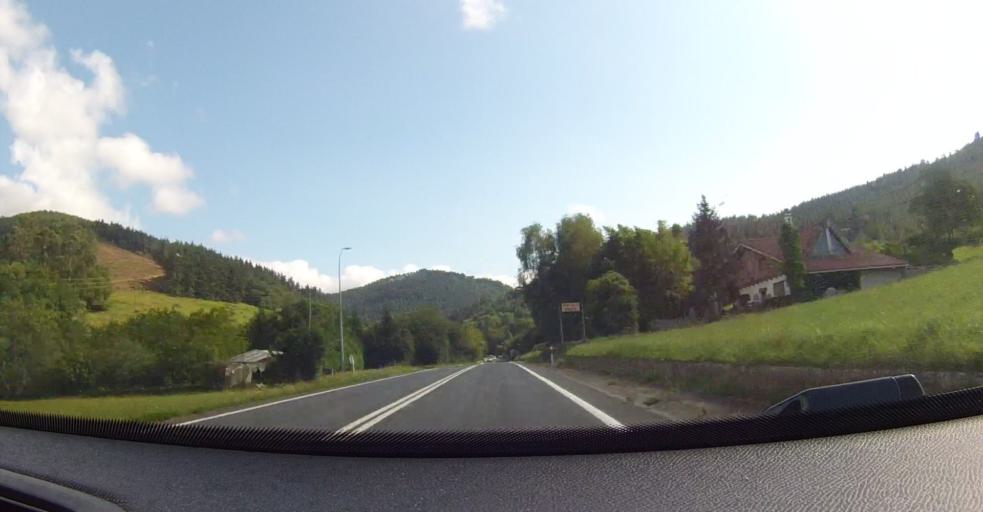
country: ES
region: Basque Country
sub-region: Bizkaia
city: Muxika
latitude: 43.2693
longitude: -2.6857
